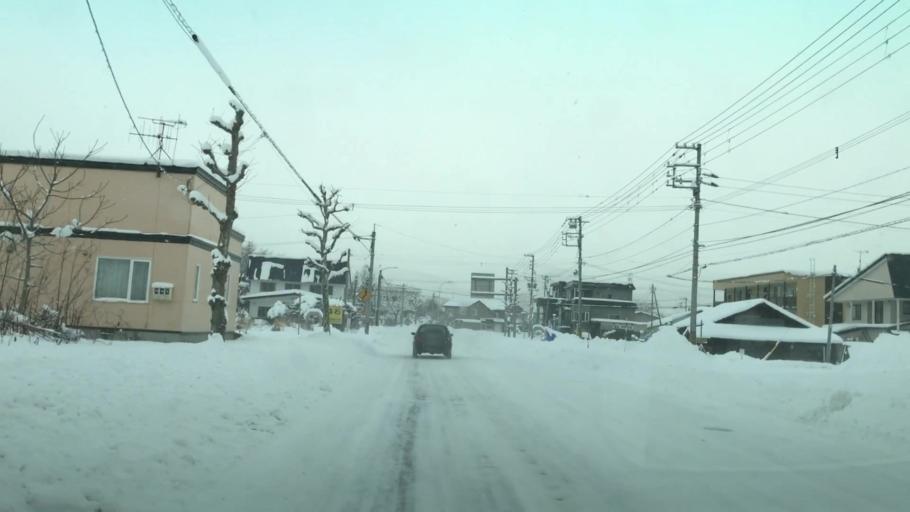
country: JP
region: Hokkaido
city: Yoichi
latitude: 43.2079
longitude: 140.7687
